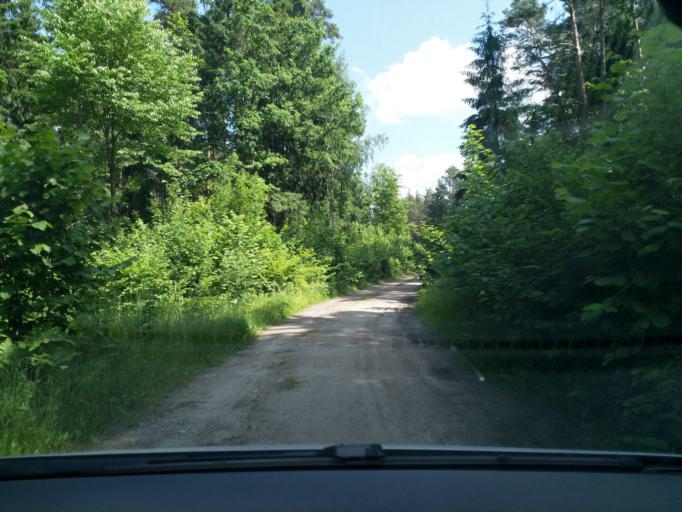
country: LV
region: Kuldigas Rajons
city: Kuldiga
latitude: 56.9702
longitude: 21.9172
